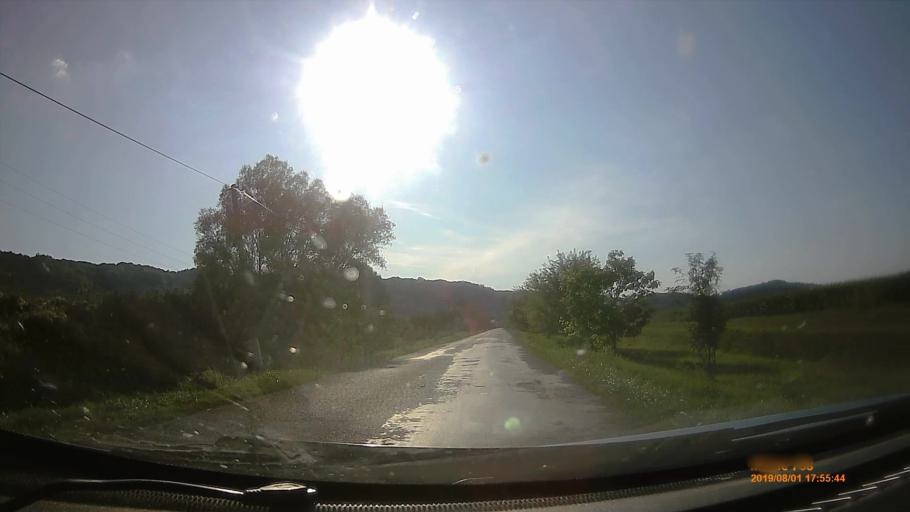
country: HU
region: Baranya
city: Sasd
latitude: 46.1942
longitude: 18.1322
